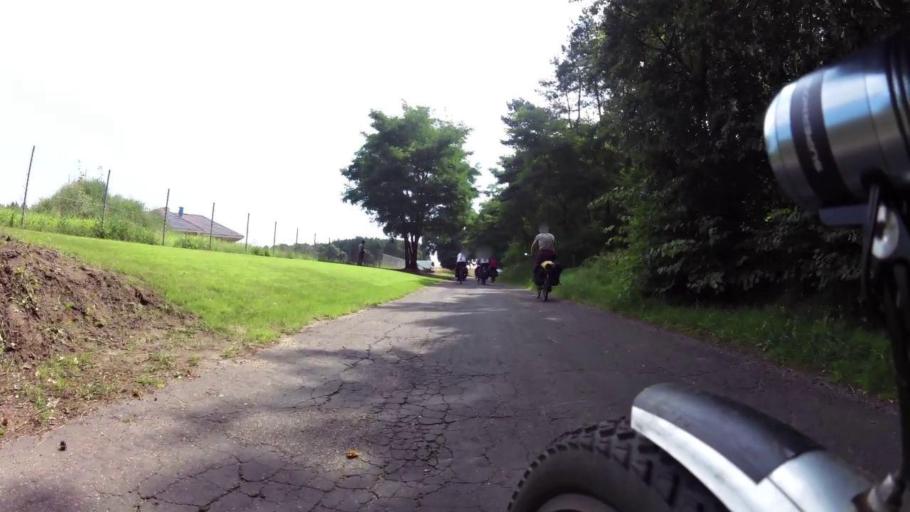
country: PL
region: West Pomeranian Voivodeship
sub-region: Powiat mysliborski
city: Boleszkowice
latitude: 52.6777
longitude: 14.6030
